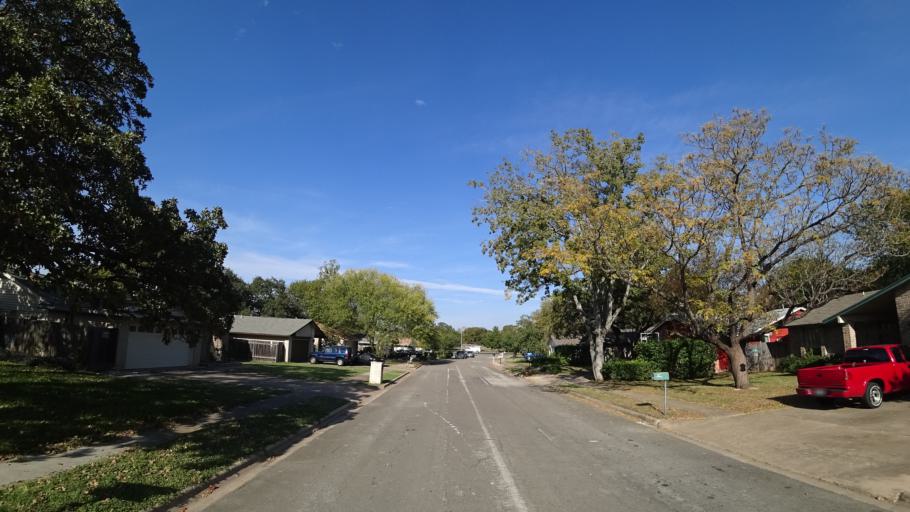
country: US
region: Texas
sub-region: Williamson County
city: Anderson Mill
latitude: 30.4567
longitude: -97.8107
